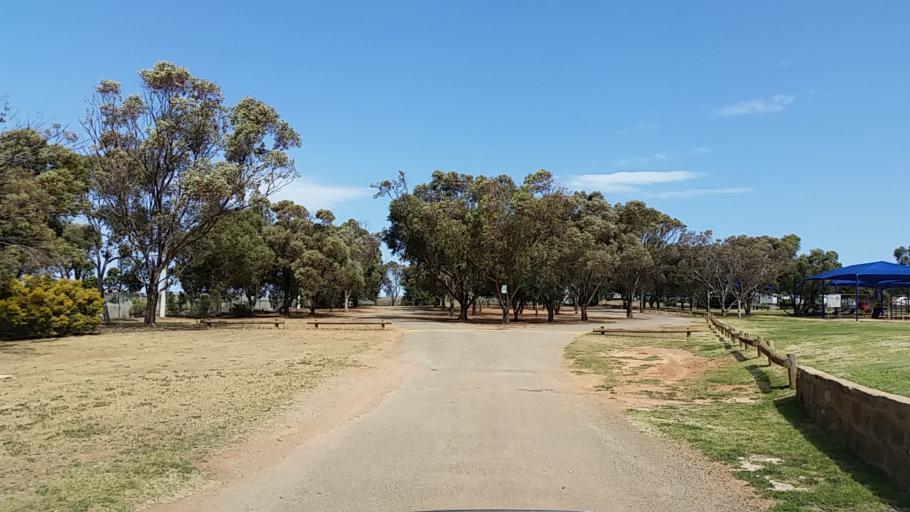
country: AU
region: South Australia
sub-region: Peterborough
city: Peterborough
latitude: -32.9794
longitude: 138.8349
